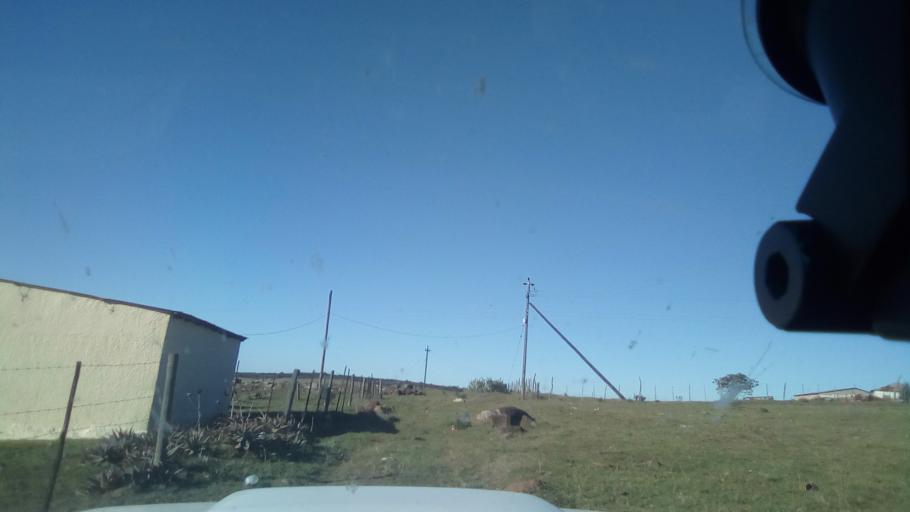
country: ZA
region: Eastern Cape
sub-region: Buffalo City Metropolitan Municipality
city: Bhisho
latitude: -32.9460
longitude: 27.2930
